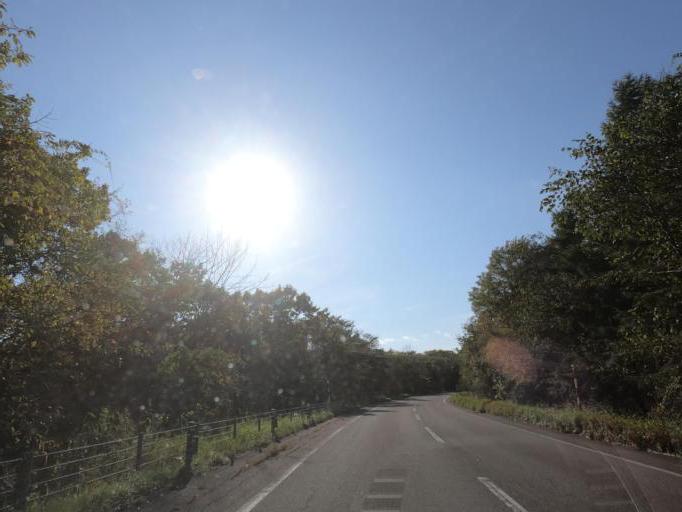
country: JP
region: Hokkaido
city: Obihiro
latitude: 42.6137
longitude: 143.4719
